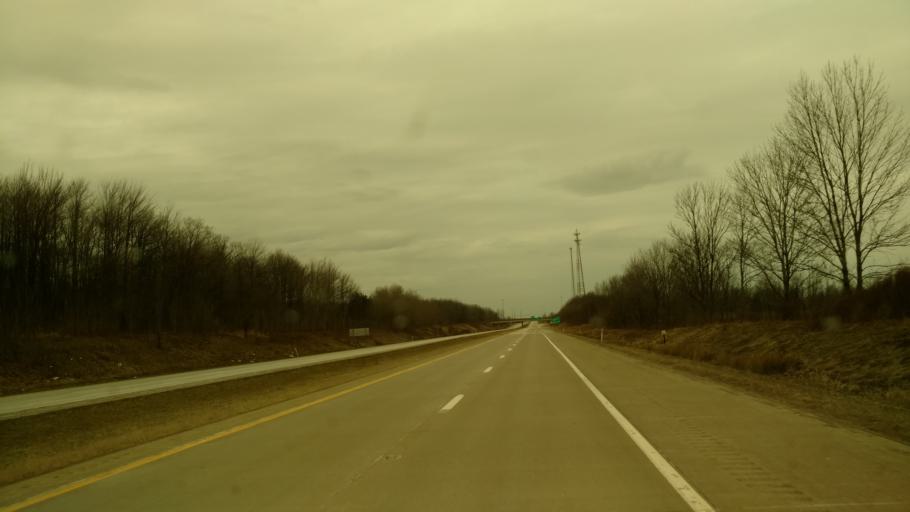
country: US
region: Pennsylvania
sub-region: Erie County
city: North East
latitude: 42.1520
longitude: -79.8762
